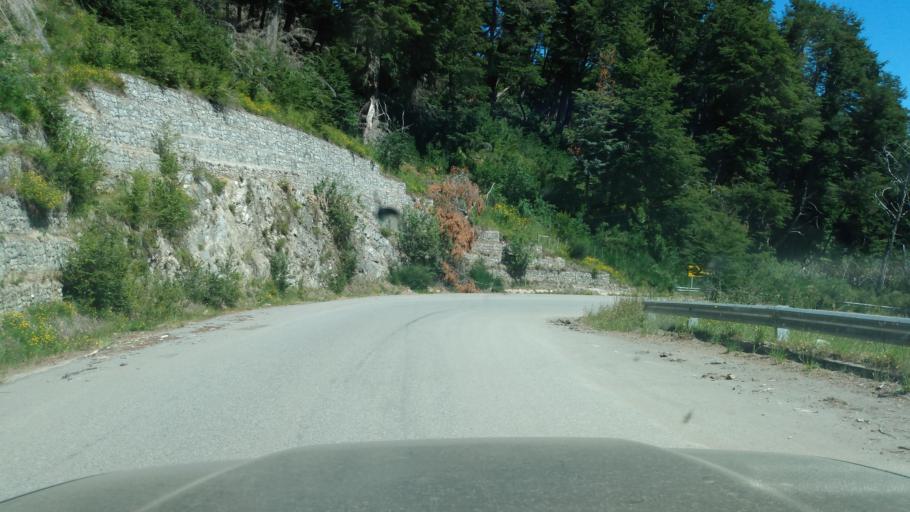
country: AR
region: Neuquen
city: Villa La Angostura
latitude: -40.6108
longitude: -71.6438
